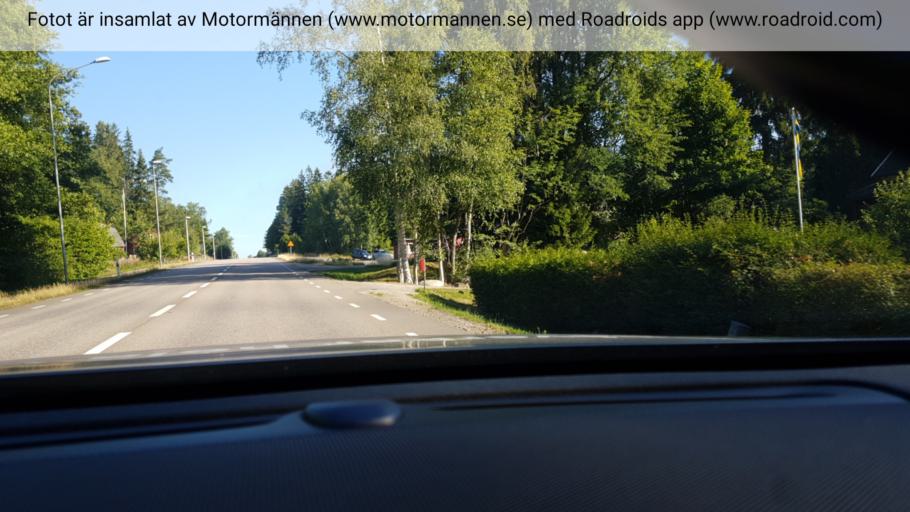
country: SE
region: Skane
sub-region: Hassleholms Kommun
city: Bjarnum
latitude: 56.3040
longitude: 13.6987
